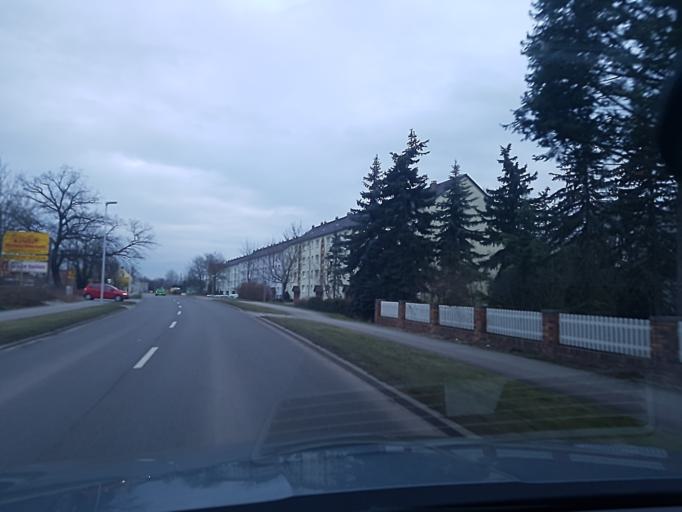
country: DE
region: Brandenburg
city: Doberlug-Kirchhain
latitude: 51.6249
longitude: 13.5627
